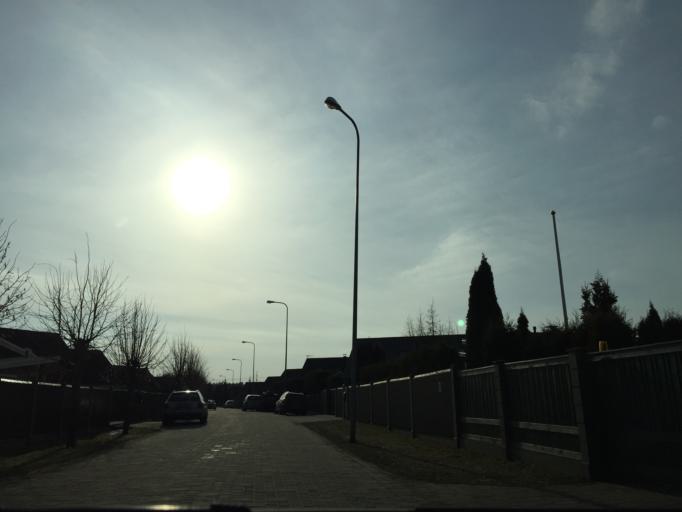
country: LV
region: Stopini
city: Ulbroka
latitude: 56.9295
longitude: 24.2601
